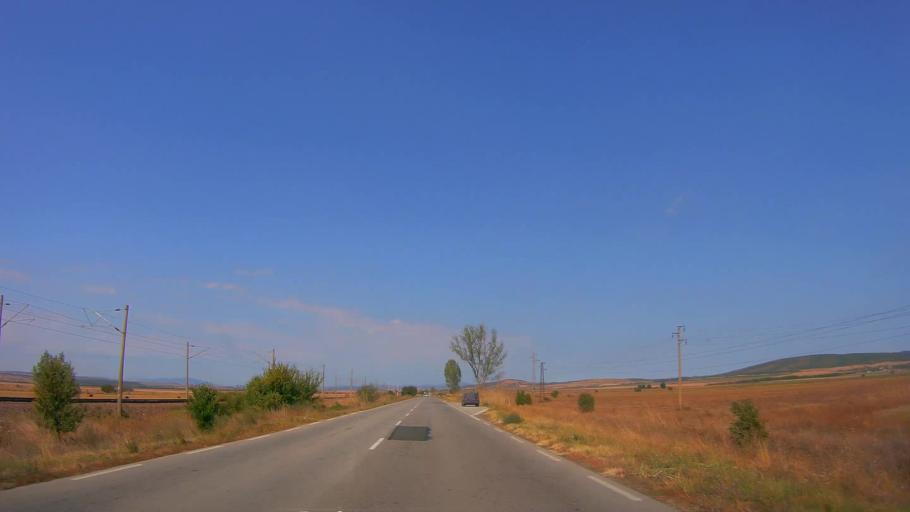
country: BG
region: Burgas
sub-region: Obshtina Karnobat
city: Karnobat
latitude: 42.6967
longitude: 26.9464
